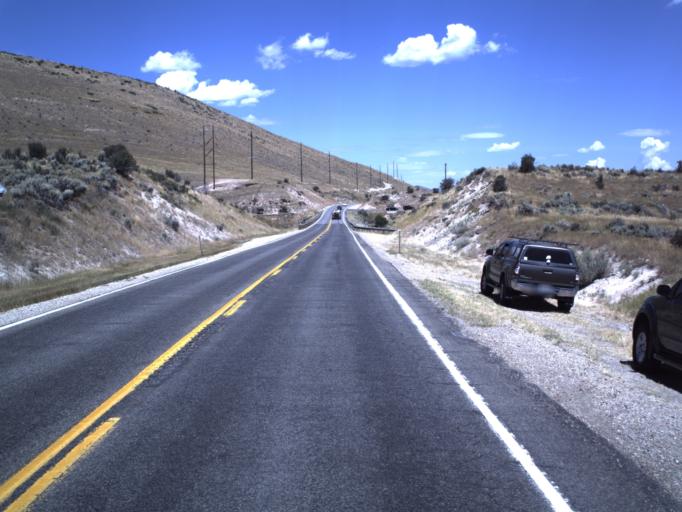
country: US
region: Utah
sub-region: Summit County
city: Oakley
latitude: 40.7737
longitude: -111.4079
